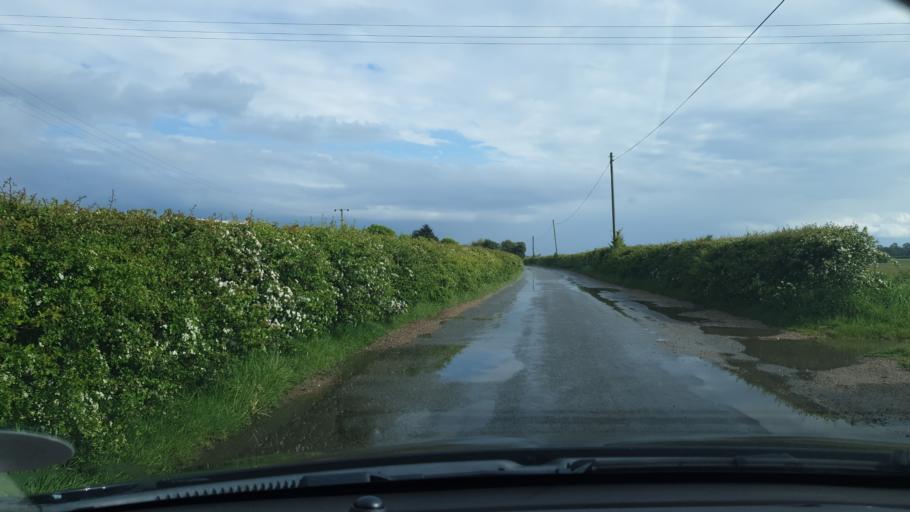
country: GB
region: England
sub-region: Essex
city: Great Bentley
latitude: 51.8483
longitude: 1.0459
